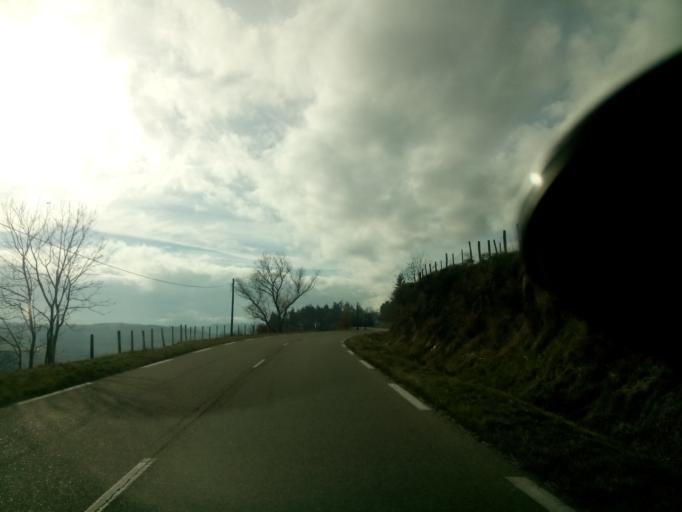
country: FR
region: Rhone-Alpes
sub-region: Departement de la Loire
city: Saint-Julien-Molin-Molette
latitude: 45.3346
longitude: 4.6428
